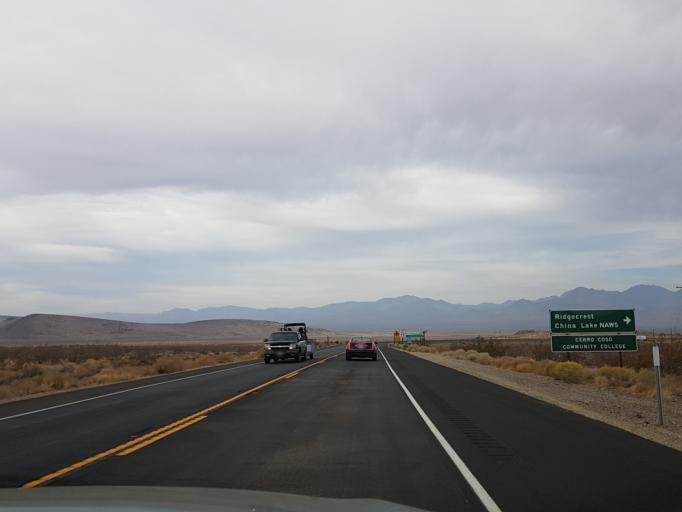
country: US
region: California
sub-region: Kern County
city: Ridgecrest
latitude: 35.5484
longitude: -117.7086
